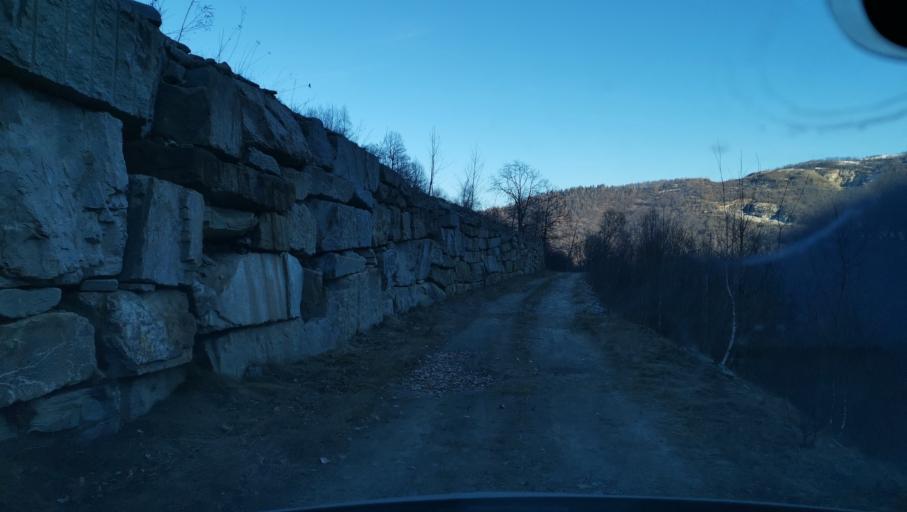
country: IT
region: Piedmont
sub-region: Provincia di Torino
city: Rora
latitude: 44.7728
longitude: 7.1920
